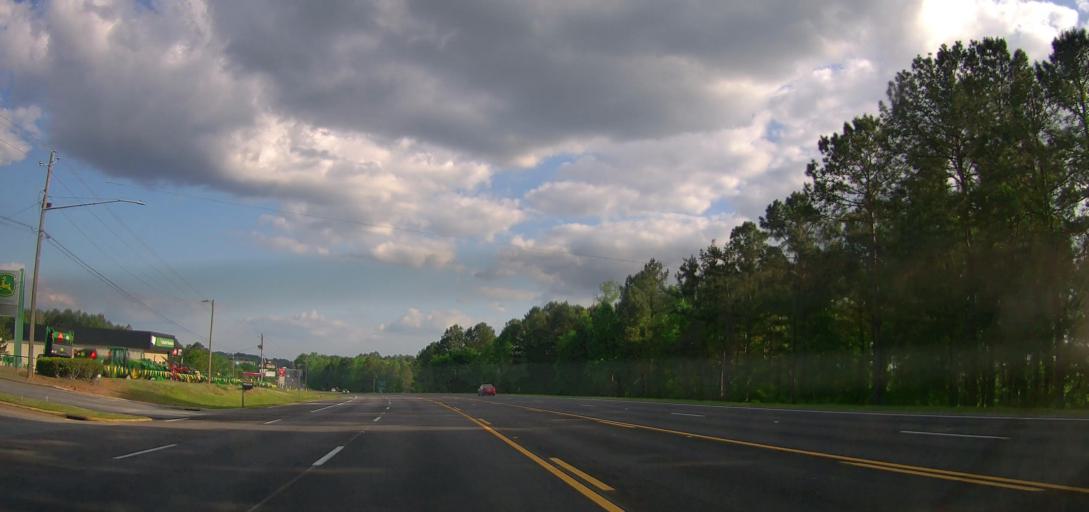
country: US
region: Georgia
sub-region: Baldwin County
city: Milledgeville
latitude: 33.1347
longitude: -83.2706
